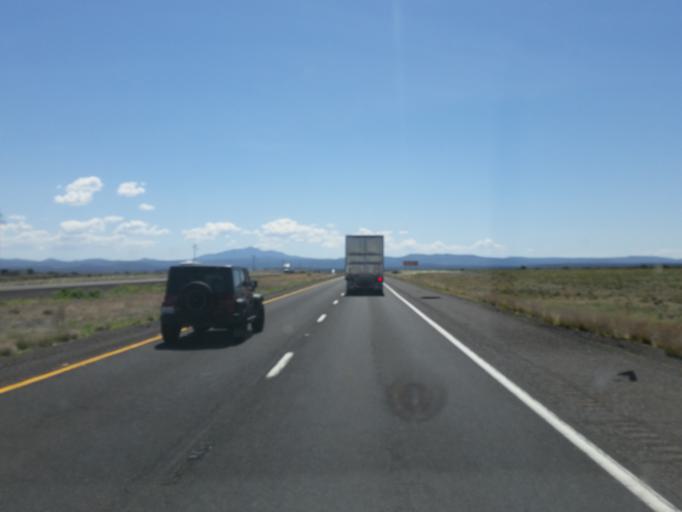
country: US
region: Arizona
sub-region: Yavapai County
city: Paulden
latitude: 35.2240
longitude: -112.5590
